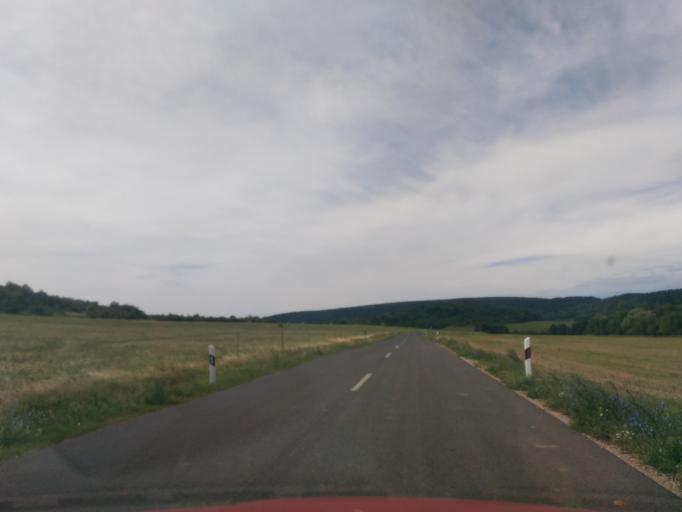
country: HU
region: Veszprem
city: Zanka
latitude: 46.9259
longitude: 17.6830
